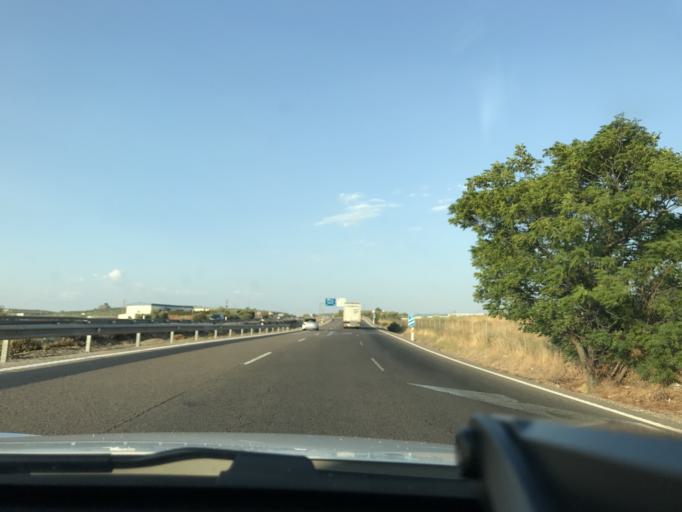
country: ES
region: Andalusia
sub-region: Provincia de Jaen
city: Bailen
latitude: 38.0924
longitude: -3.8131
